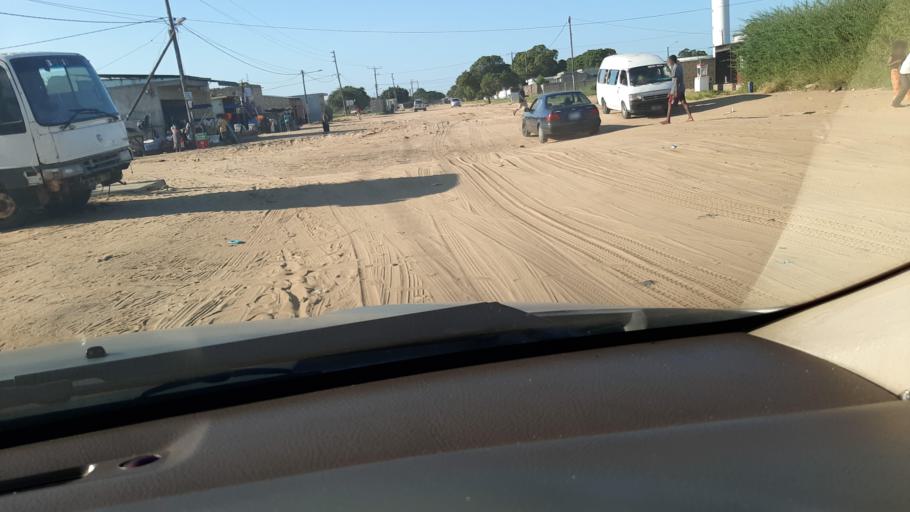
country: MZ
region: Maputo City
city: Maputo
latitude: -25.7890
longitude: 32.5523
